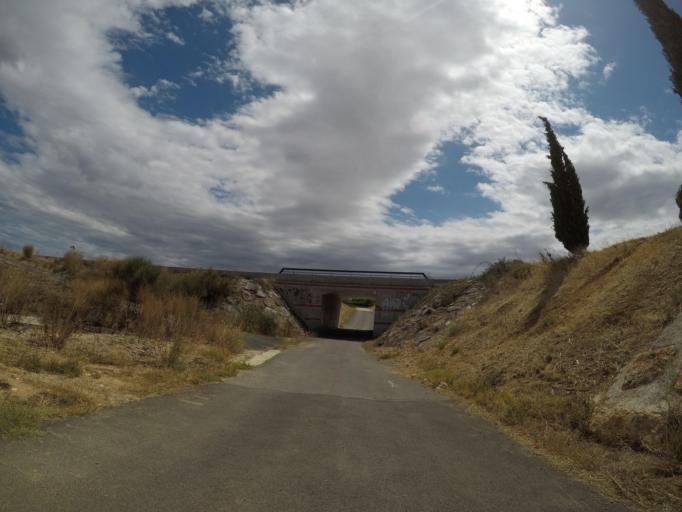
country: FR
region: Languedoc-Roussillon
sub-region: Departement des Pyrenees-Orientales
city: Baho
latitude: 42.7118
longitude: 2.8169
